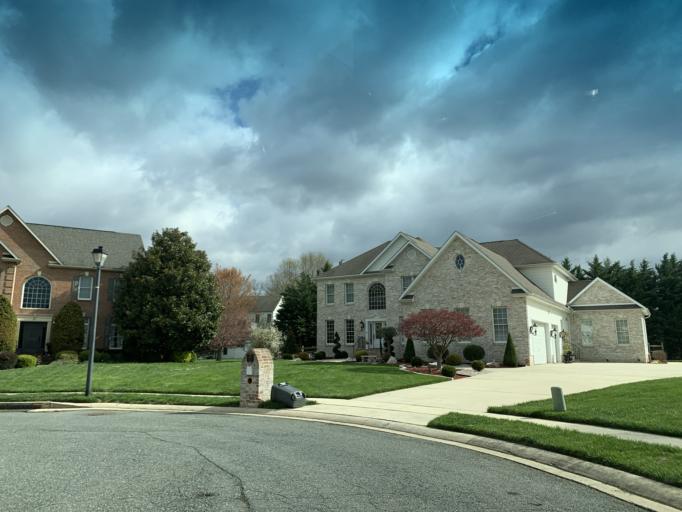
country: US
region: Maryland
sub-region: Harford County
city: South Bel Air
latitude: 39.5555
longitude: -76.3073
